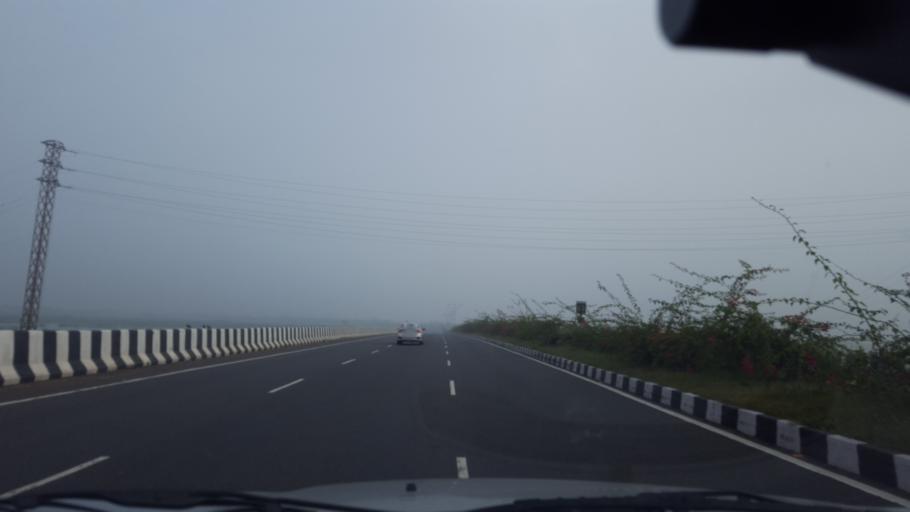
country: IN
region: Andhra Pradesh
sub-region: Prakasam
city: Ongole
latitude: 15.4979
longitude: 80.0687
